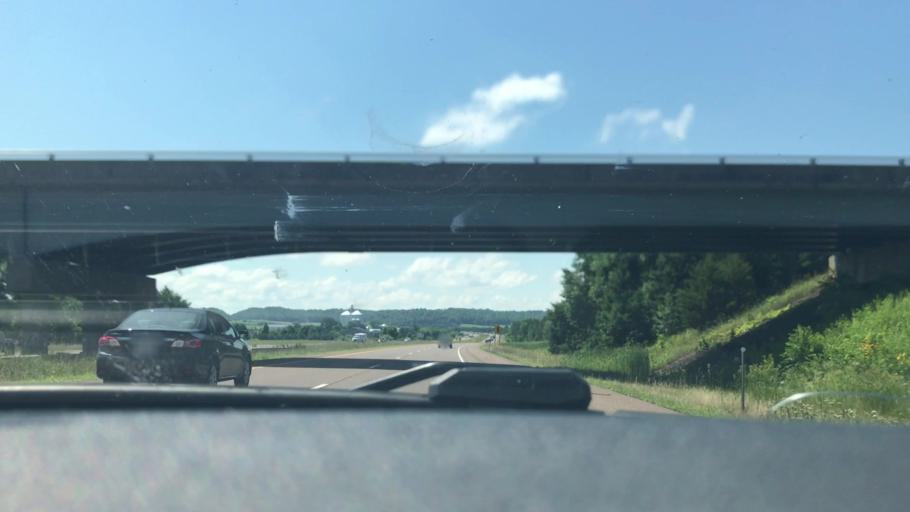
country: US
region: Wisconsin
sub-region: Chippewa County
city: Chippewa Falls
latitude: 45.0004
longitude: -91.4421
